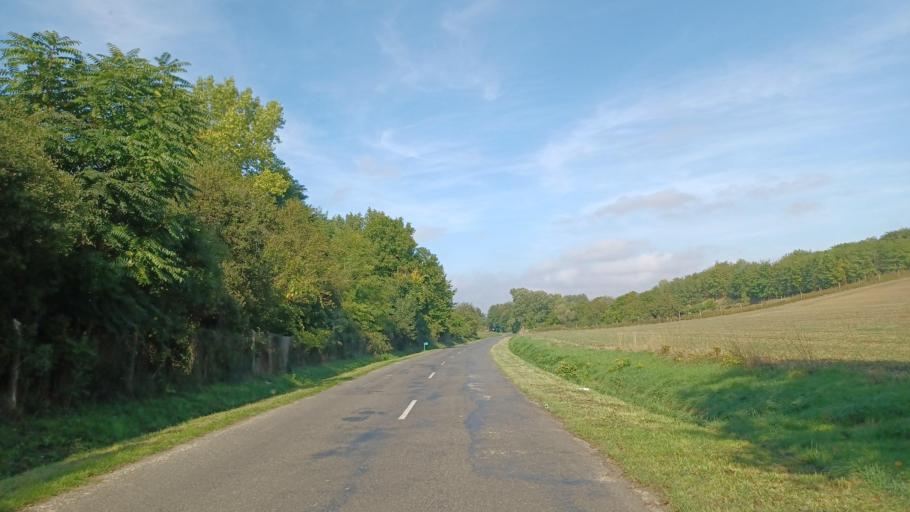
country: HU
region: Tolna
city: Pincehely
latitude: 46.6889
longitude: 18.4591
